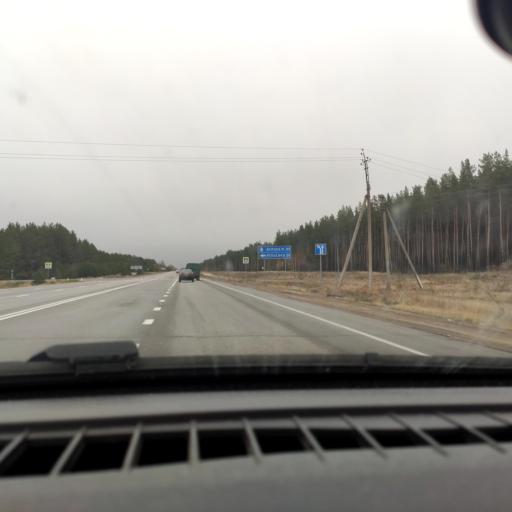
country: RU
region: Voronezj
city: Uryv-Pokrovka
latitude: 51.0479
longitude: 38.9831
